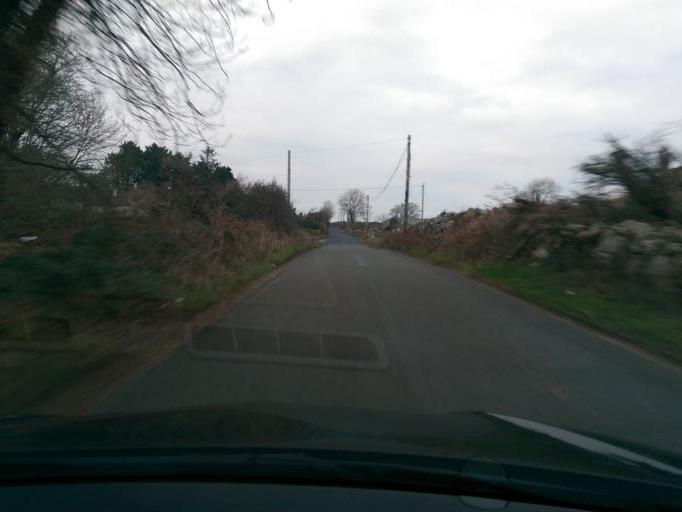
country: IE
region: Connaught
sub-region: County Galway
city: Bearna
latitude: 53.2582
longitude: -9.1532
